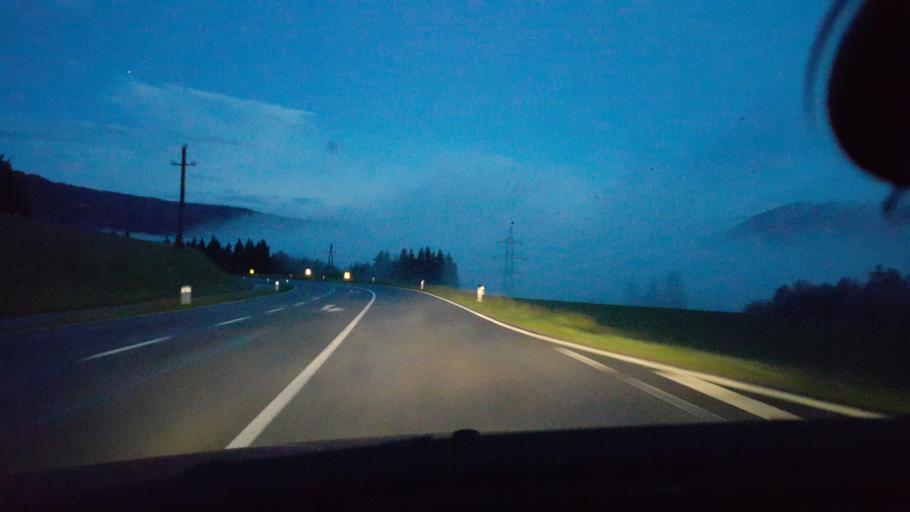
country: AT
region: Carinthia
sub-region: Politischer Bezirk Volkermarkt
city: Ruden
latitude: 46.6370
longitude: 14.7784
